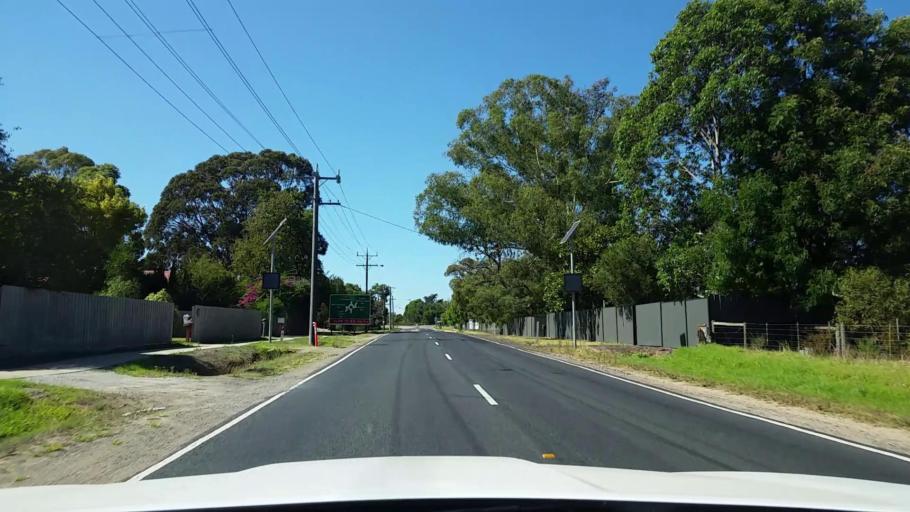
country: AU
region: Victoria
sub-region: Mornington Peninsula
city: Langwarrin South
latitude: -38.1987
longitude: 145.1789
